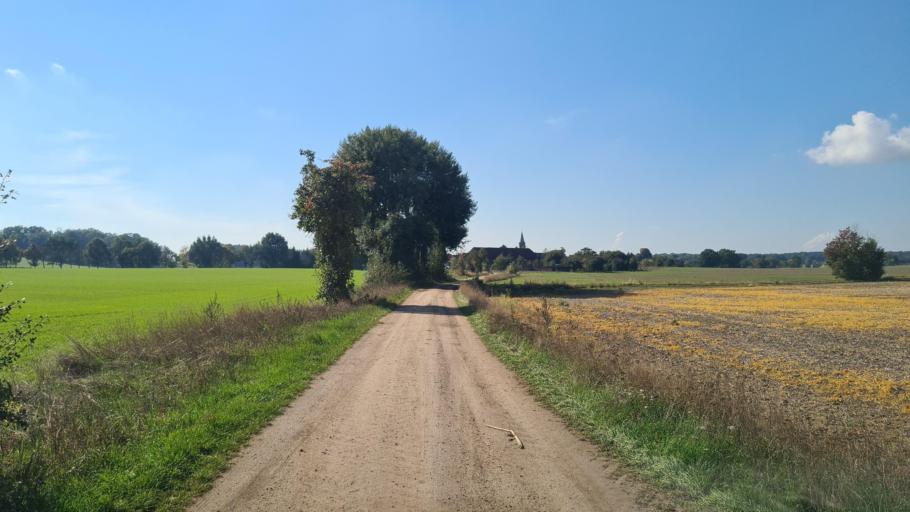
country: DE
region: Brandenburg
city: Lebusa
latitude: 51.8279
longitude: 13.4619
